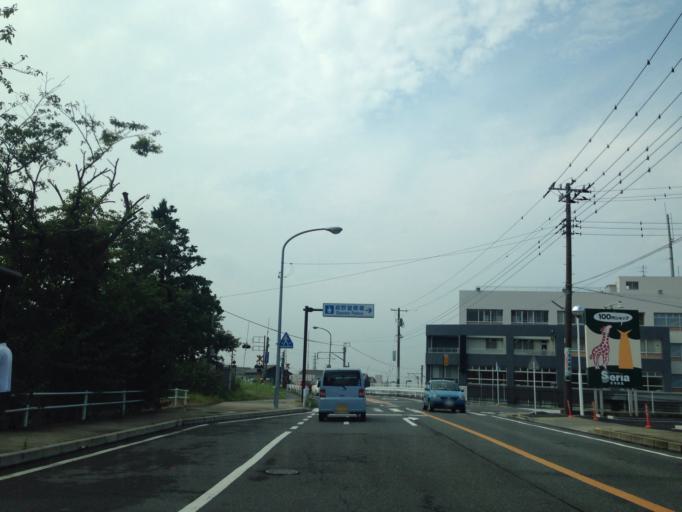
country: JP
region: Shizuoka
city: Mishima
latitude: 35.1676
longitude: 138.9069
